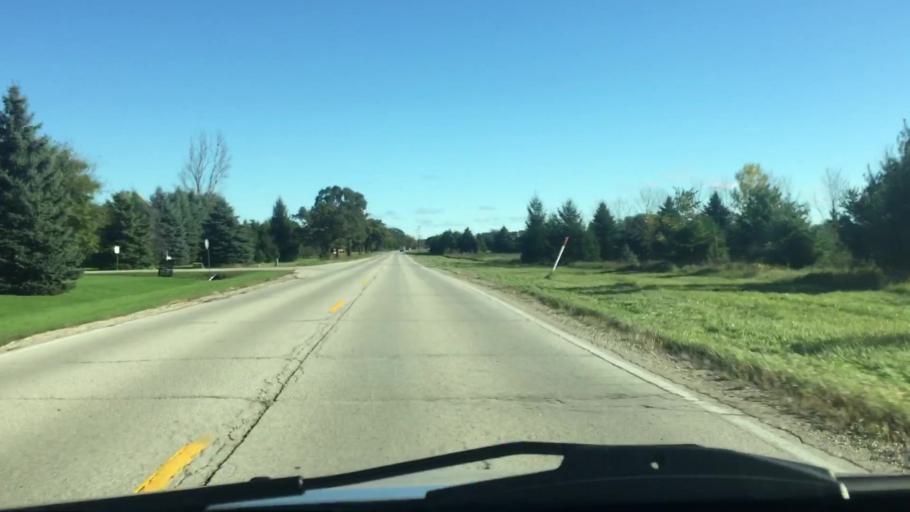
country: US
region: Wisconsin
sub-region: Waukesha County
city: North Prairie
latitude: 42.9706
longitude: -88.4014
